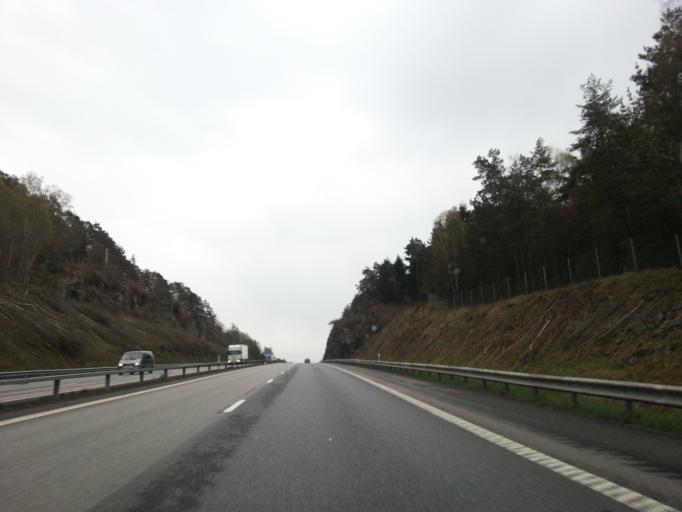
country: SE
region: Halland
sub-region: Kungsbacka Kommun
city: Frillesas
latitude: 57.3142
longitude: 12.2107
